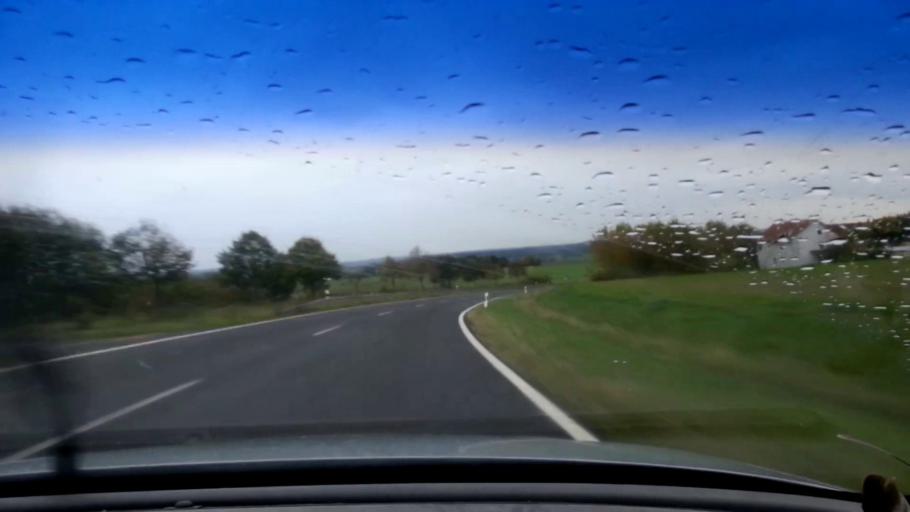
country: DE
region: Bavaria
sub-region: Upper Franconia
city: Priesendorf
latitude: 49.8664
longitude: 10.7174
